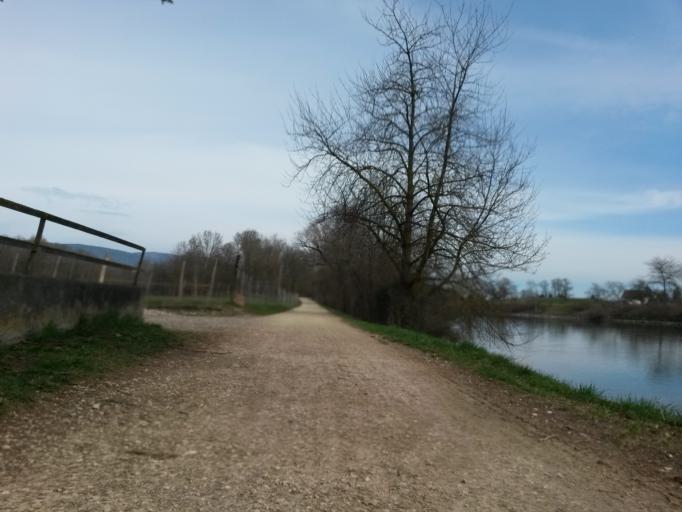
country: CH
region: Bern
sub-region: Biel/Bienne District
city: Orpund
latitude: 47.1317
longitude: 7.3032
